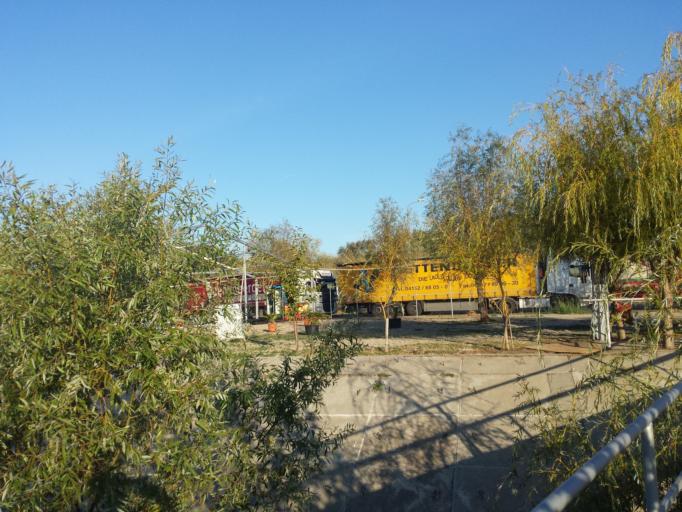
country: BG
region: Pleven
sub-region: Obshtina Nikopol
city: Nikopol
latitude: 43.7124
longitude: 24.8882
